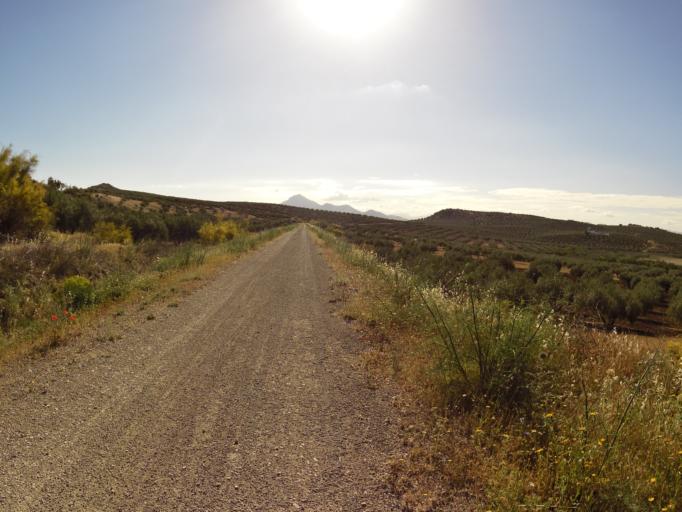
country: ES
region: Andalusia
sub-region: Province of Cordoba
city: Luque
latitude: 37.5831
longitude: -4.2055
